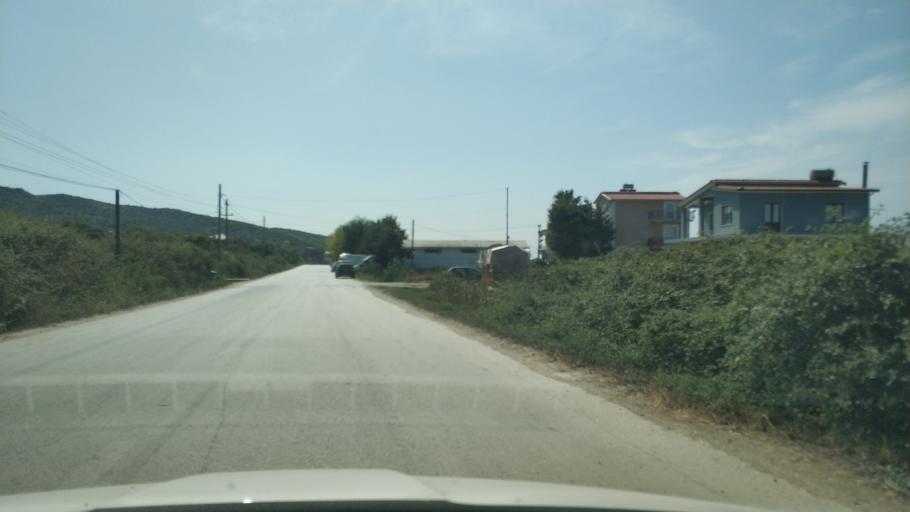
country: AL
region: Fier
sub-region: Rrethi i Lushnjes
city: Grabjan
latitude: 40.9460
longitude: 19.5370
